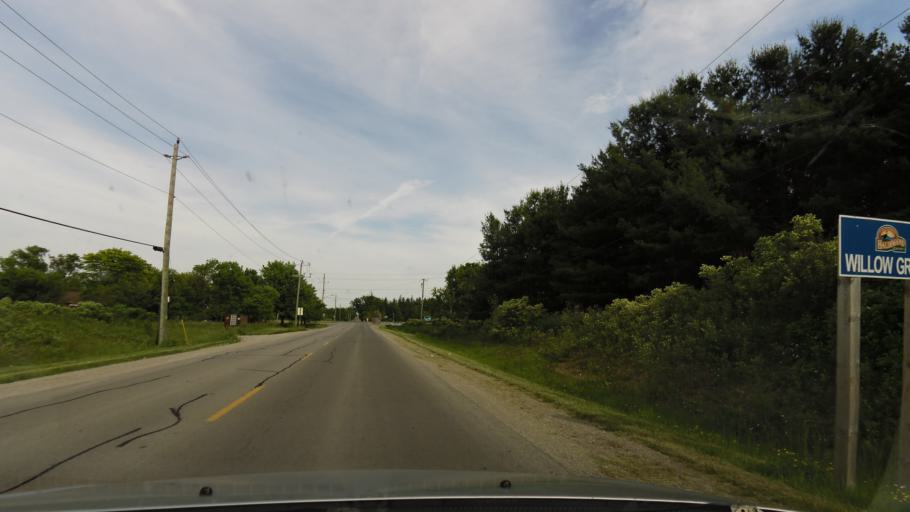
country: CA
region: Ontario
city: Ancaster
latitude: 43.0246
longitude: -79.9979
